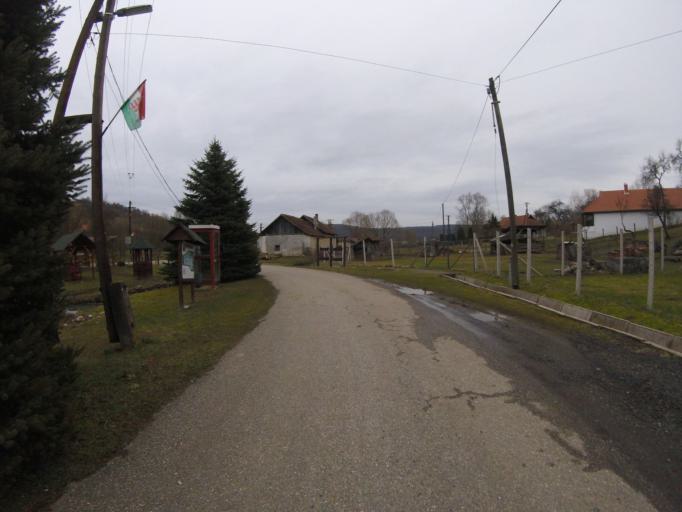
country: HU
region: Borsod-Abauj-Zemplen
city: Rudabanya
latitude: 48.4453
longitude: 20.6053
